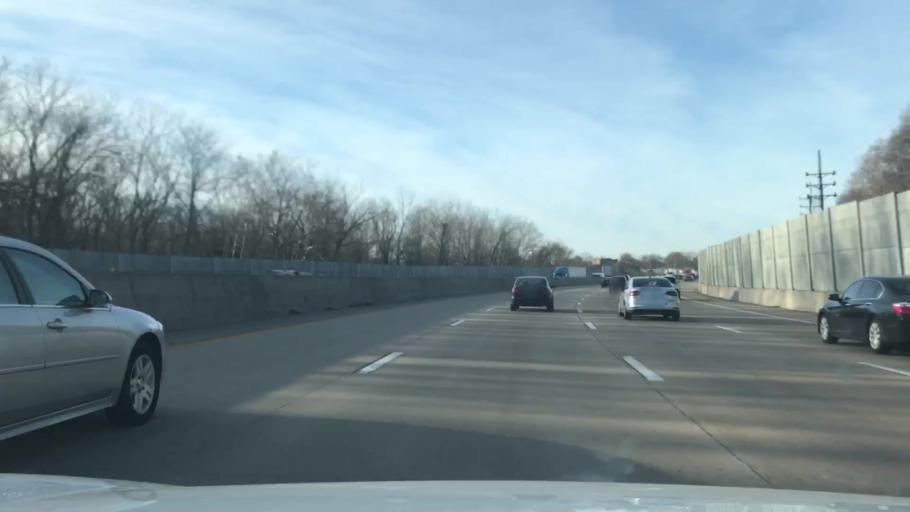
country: US
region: Missouri
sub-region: Saint Louis County
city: Ladue
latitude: 38.6325
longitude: -90.3866
